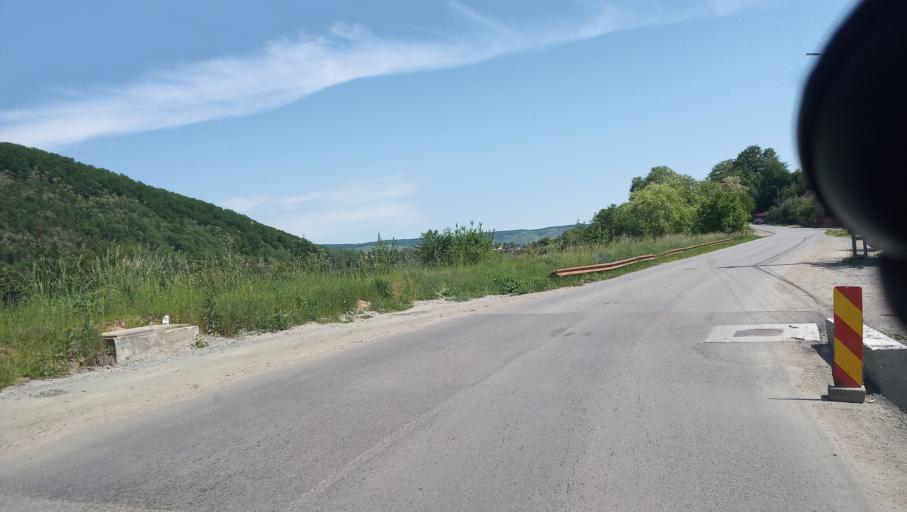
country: RO
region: Cluj
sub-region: Comuna Gilau
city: Gilau
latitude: 46.7361
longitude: 23.3617
